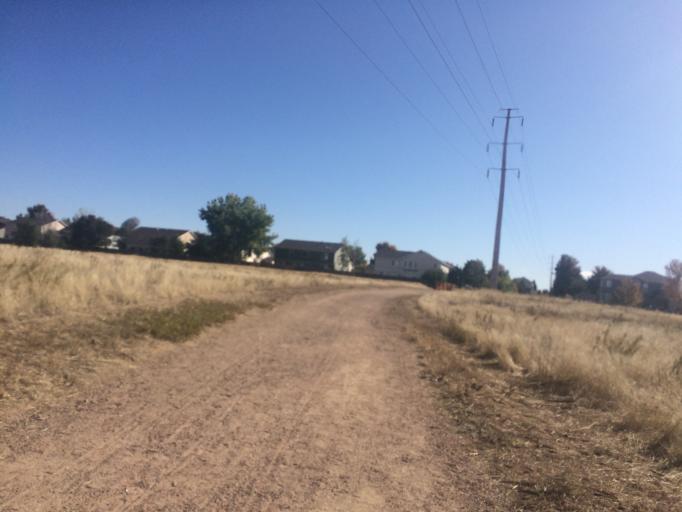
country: US
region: Colorado
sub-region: Broomfield County
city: Broomfield
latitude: 39.8791
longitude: -105.0719
